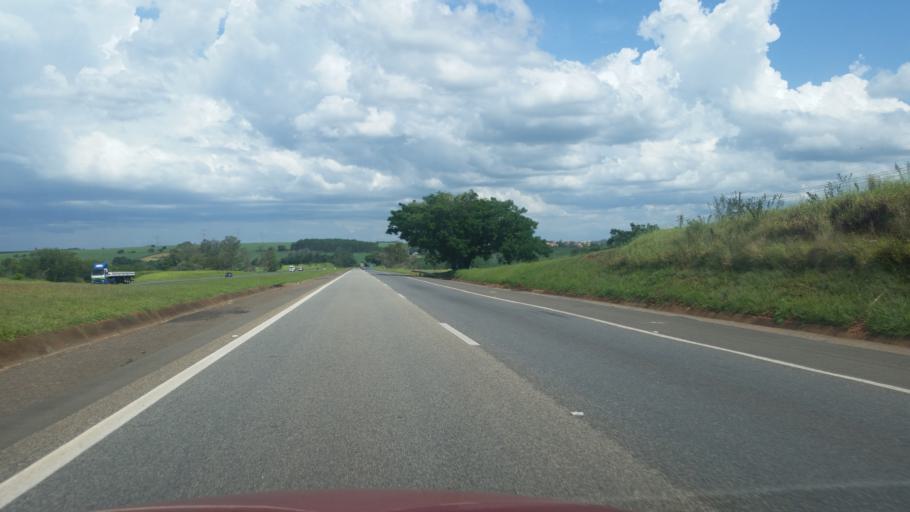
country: BR
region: Sao Paulo
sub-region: Tatui
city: Tatui
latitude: -23.2615
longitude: -47.8493
